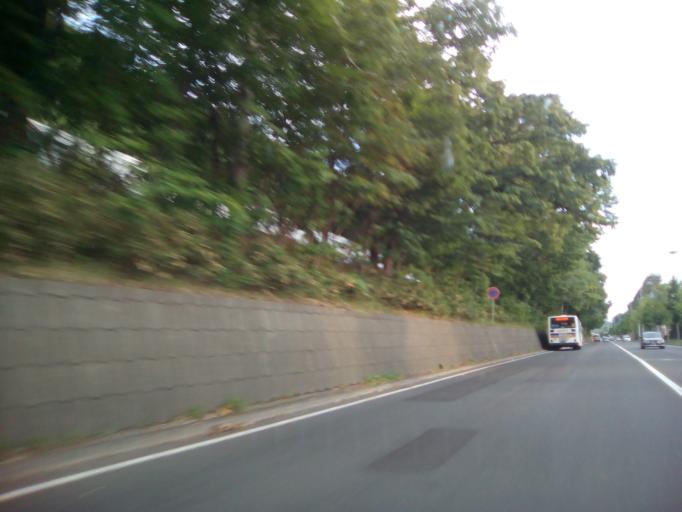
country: JP
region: Hokkaido
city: Sapporo
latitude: 42.9958
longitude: 141.3589
